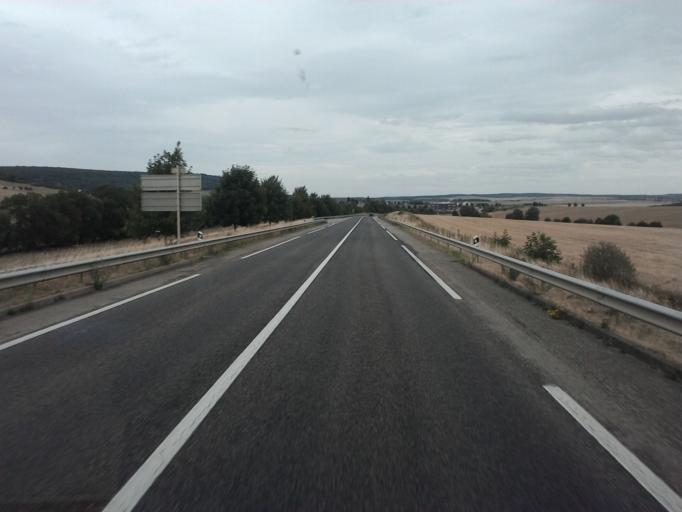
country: FR
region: Lorraine
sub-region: Departement de Meurthe-et-Moselle
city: Bainville-sur-Madon
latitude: 48.5798
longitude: 6.0408
